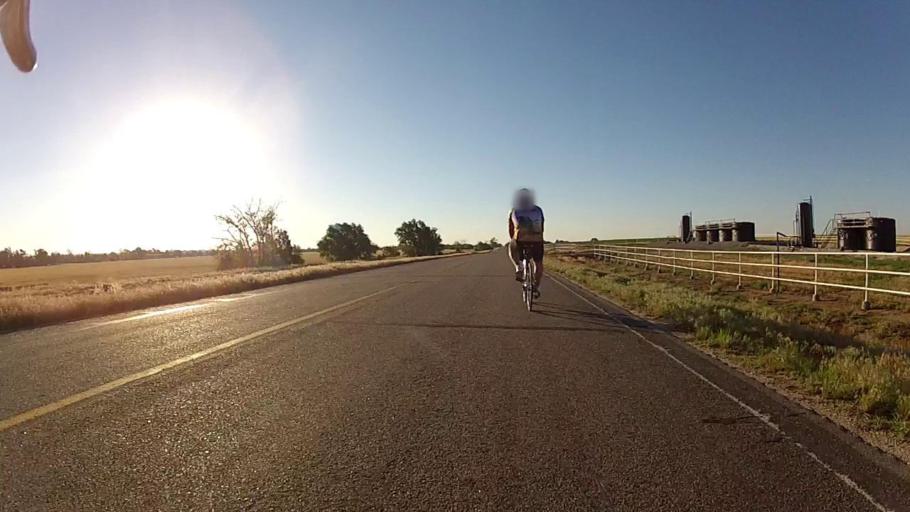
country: US
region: Kansas
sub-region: Ford County
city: Dodge City
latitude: 37.7188
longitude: -99.9451
